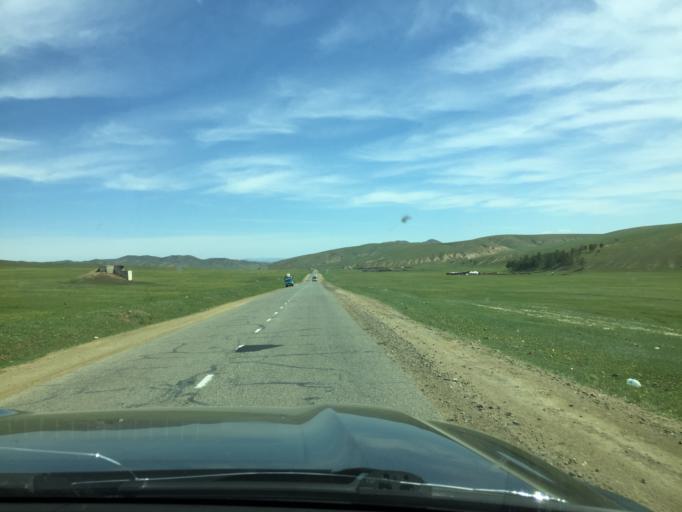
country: MN
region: Central Aimak
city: Javhlant
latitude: 48.6587
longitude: 106.1186
